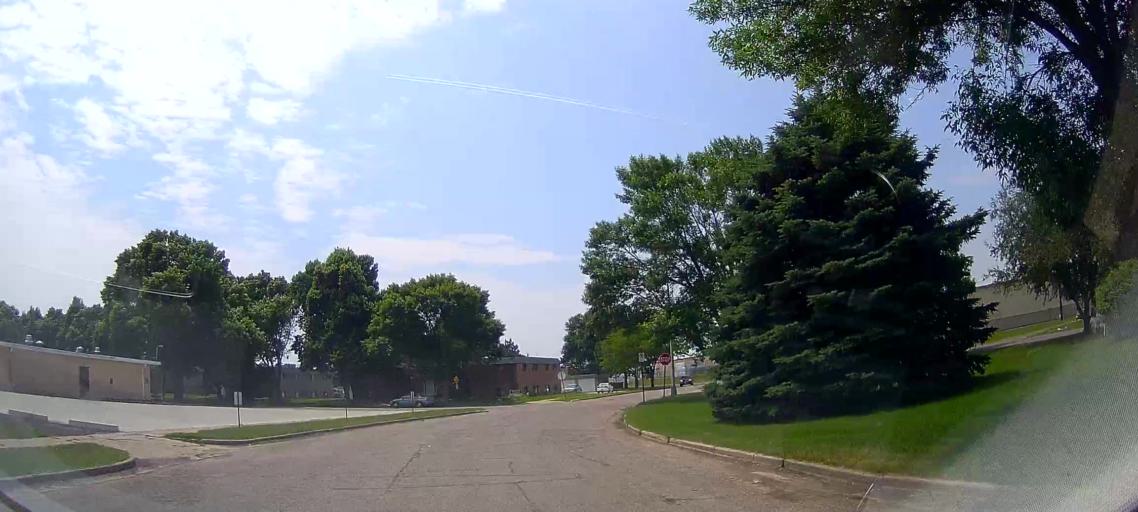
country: US
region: South Dakota
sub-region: Minnehaha County
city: Sioux Falls
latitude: 43.5071
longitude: -96.7456
